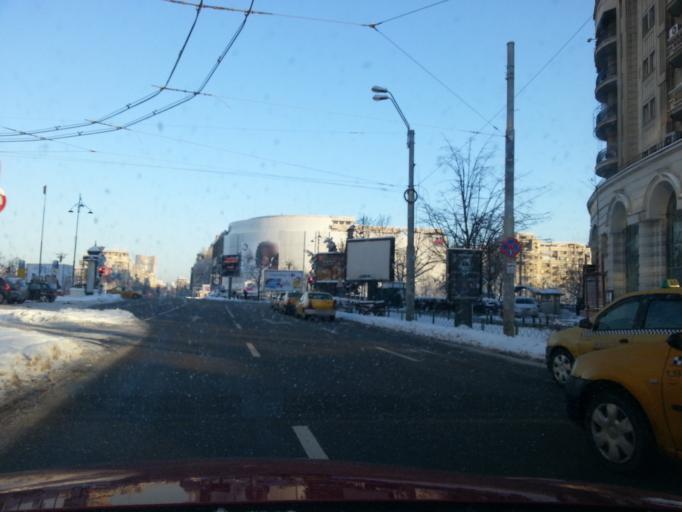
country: RO
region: Bucuresti
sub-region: Municipiul Bucuresti
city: Bucharest
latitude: 44.4250
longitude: 26.1043
